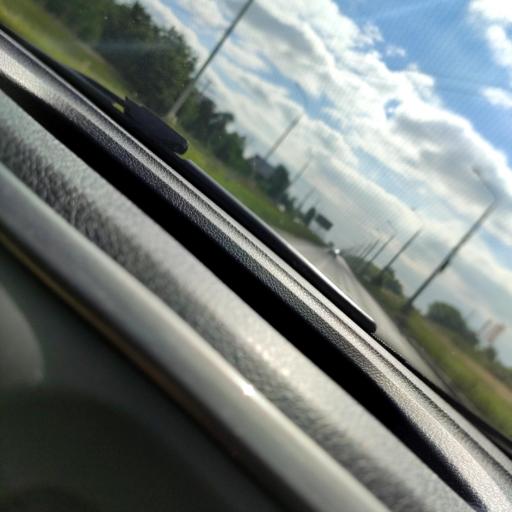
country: RU
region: Samara
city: Tol'yatti
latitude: 53.5590
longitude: 49.3216
